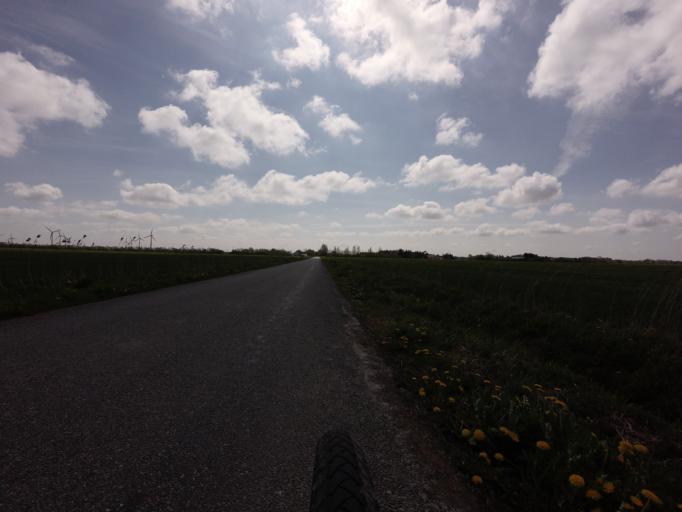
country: DK
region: North Denmark
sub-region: Jammerbugt Kommune
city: Brovst
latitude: 57.1342
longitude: 9.5222
